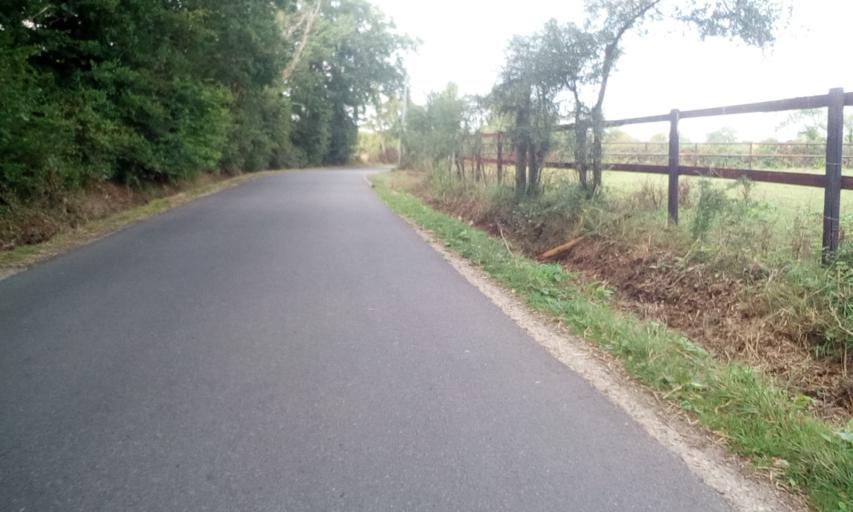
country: FR
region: Lower Normandy
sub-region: Departement du Calvados
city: Moult
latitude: 49.1257
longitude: -0.1316
